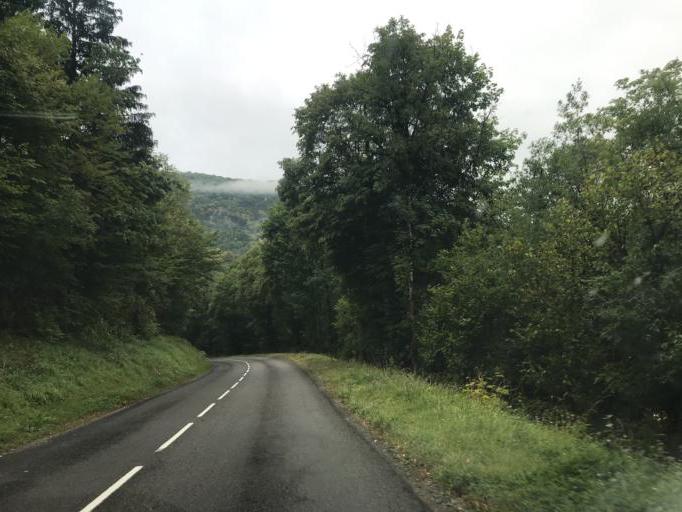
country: FR
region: Rhone-Alpes
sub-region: Departement de l'Ain
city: Dortan
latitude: 46.3228
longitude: 5.6508
